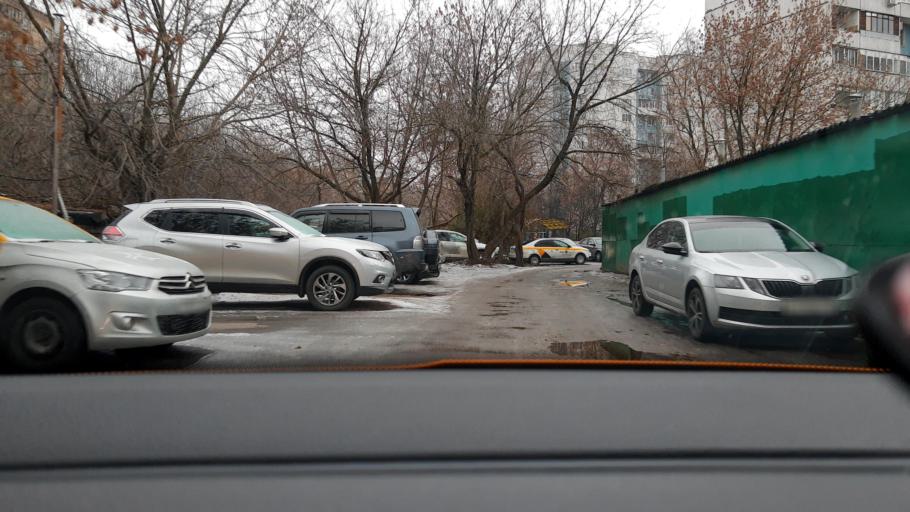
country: RU
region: Moscow
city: Shchukino
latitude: 55.7982
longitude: 37.4590
